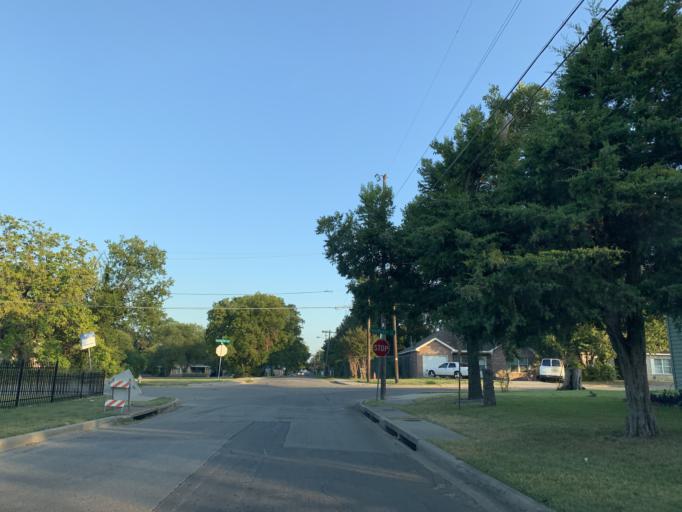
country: US
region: Texas
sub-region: Dallas County
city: Dallas
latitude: 32.7061
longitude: -96.7840
